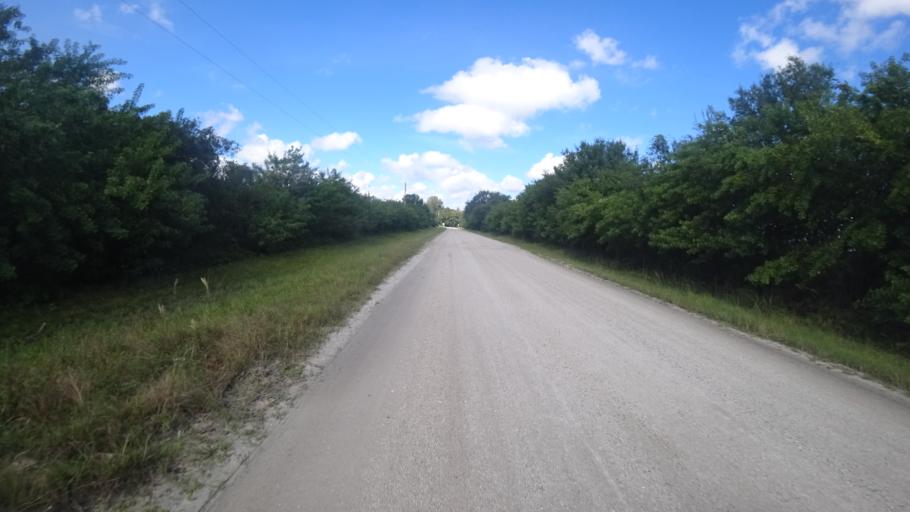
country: US
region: Florida
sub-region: Sarasota County
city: Lake Sarasota
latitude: 27.3670
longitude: -82.1393
